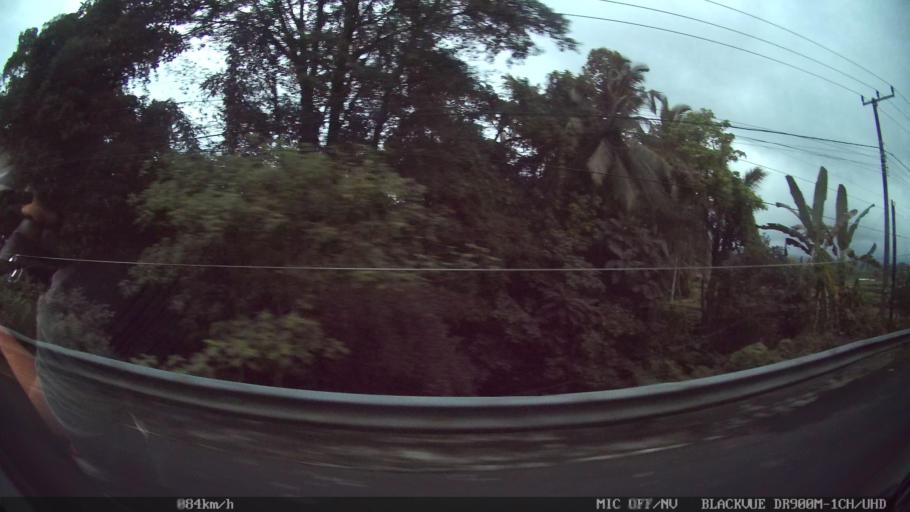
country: ID
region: Bali
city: Penebel
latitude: -8.4090
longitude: 115.1457
